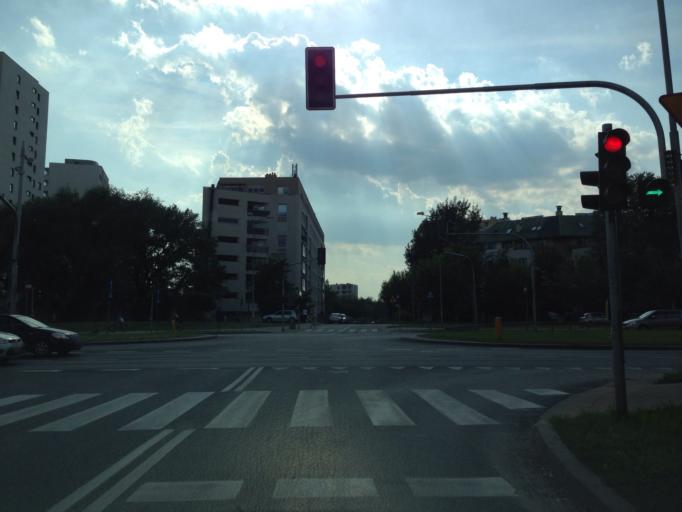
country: PL
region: Masovian Voivodeship
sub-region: Warszawa
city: Bemowo
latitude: 52.2421
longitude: 20.9131
